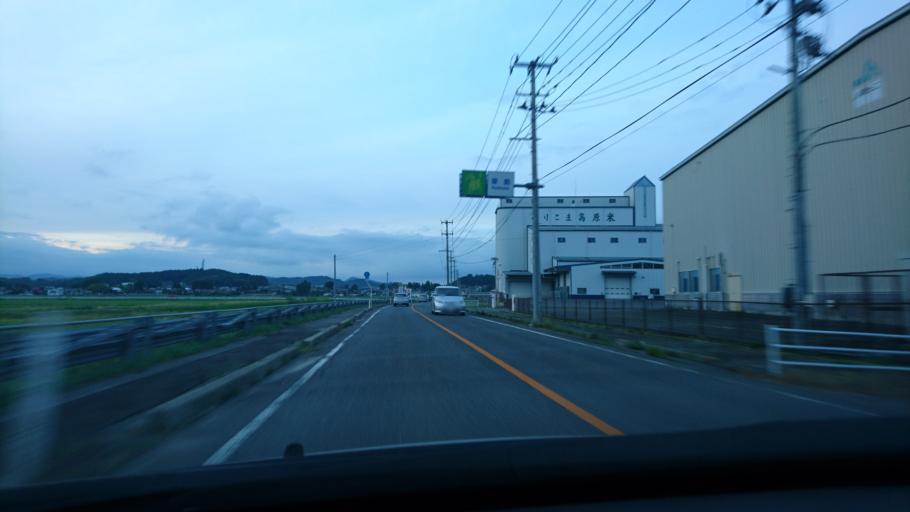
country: JP
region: Iwate
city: Ichinoseki
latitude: 38.8018
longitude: 140.9811
